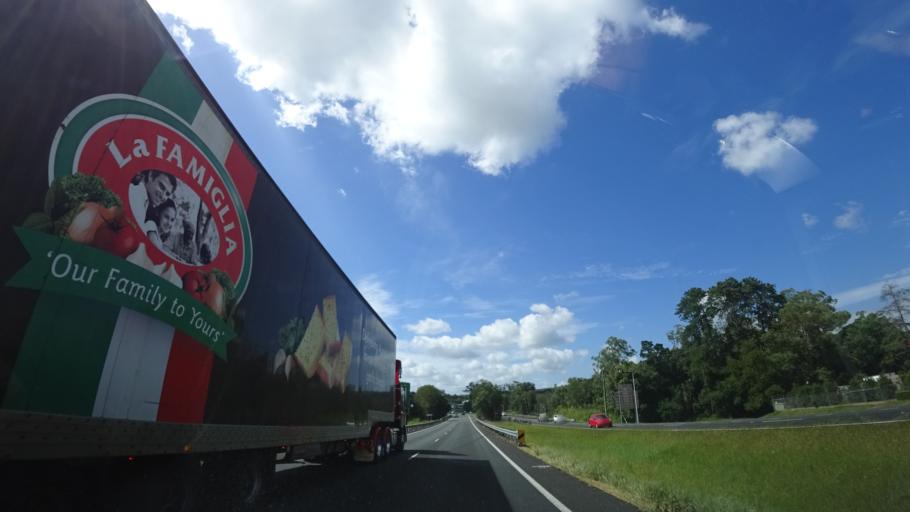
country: AU
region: Queensland
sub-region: Sunshine Coast
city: Woombye
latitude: -26.6834
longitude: 153.0031
